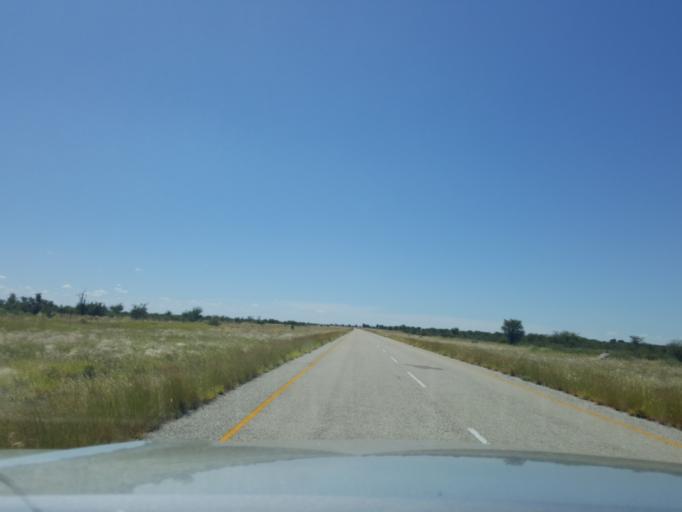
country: BW
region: Central
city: Gweta
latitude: -20.2208
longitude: 25.0470
